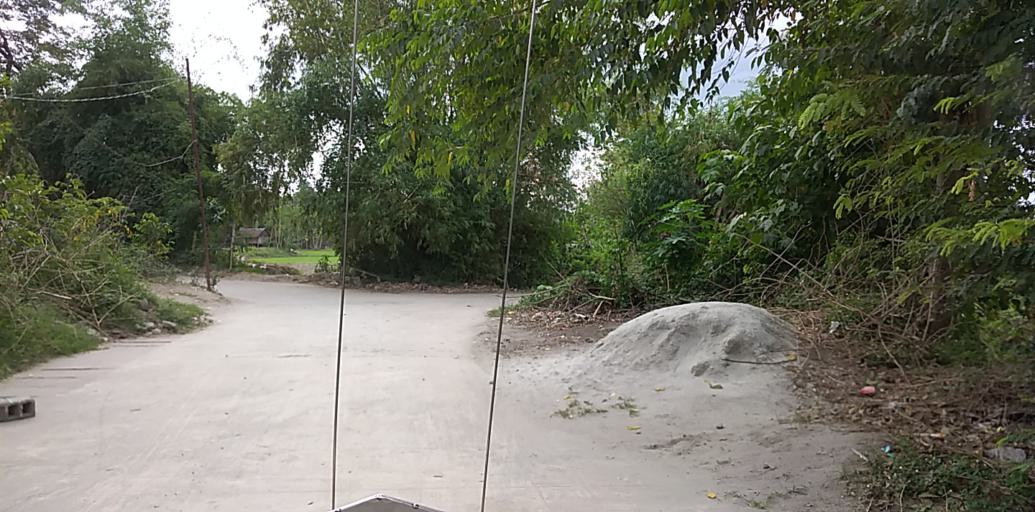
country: PH
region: Central Luzon
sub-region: Province of Pampanga
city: Porac
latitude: 15.0617
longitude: 120.5332
